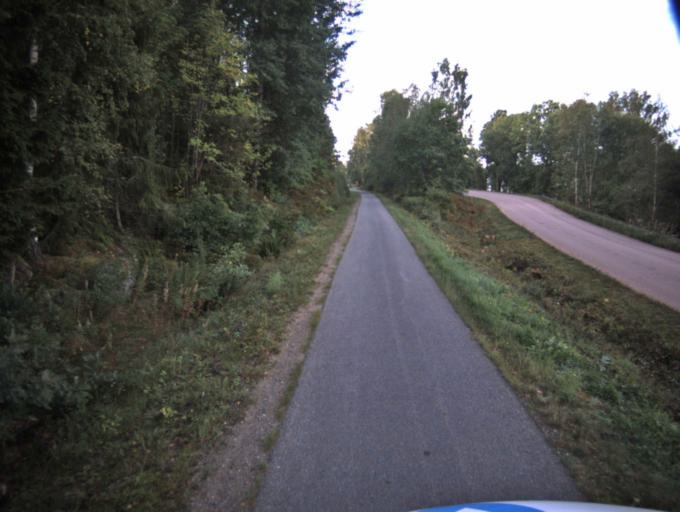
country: SE
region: Vaestra Goetaland
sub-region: Ulricehamns Kommun
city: Ulricehamn
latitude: 57.7529
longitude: 13.3955
